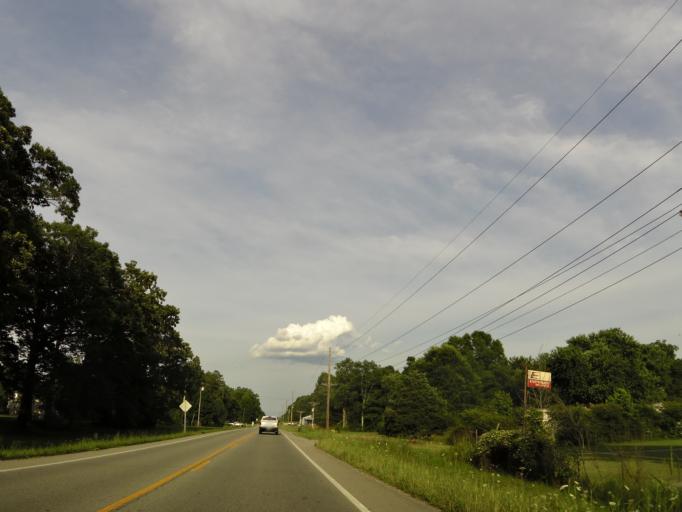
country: US
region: Tennessee
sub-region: Dickson County
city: Dickson
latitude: 36.0902
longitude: -87.4941
